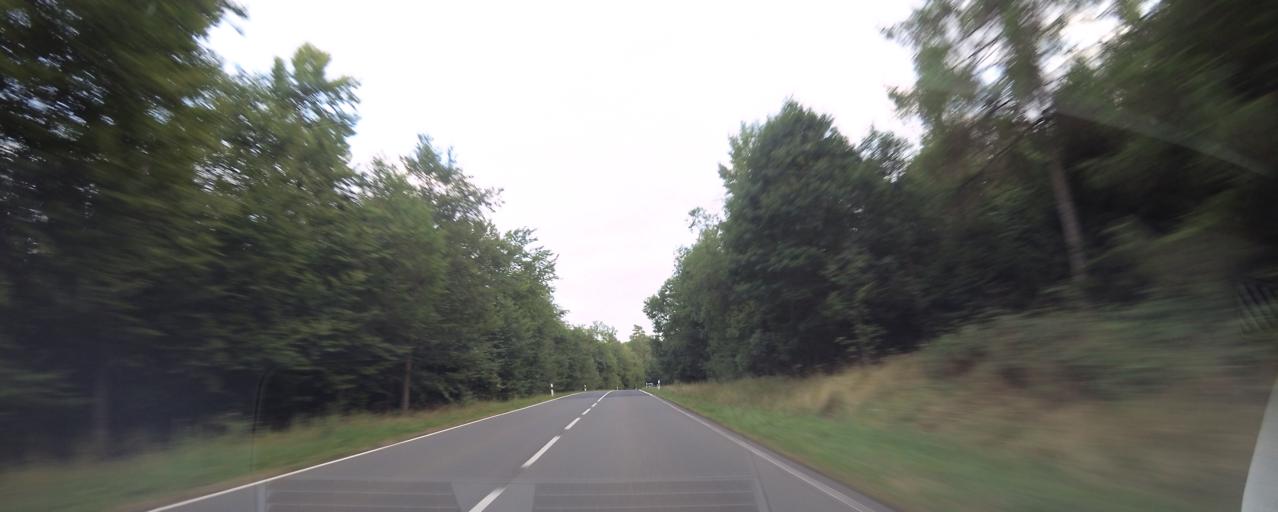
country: DE
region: Rheinland-Pfalz
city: Zemmer
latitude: 49.9165
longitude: 6.7064
